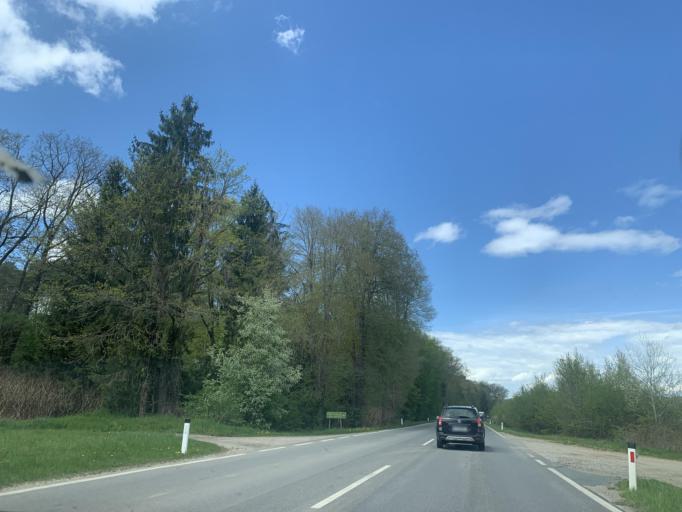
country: AT
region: Styria
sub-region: Politischer Bezirk Leibnitz
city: Lang
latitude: 46.8258
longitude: 15.5217
